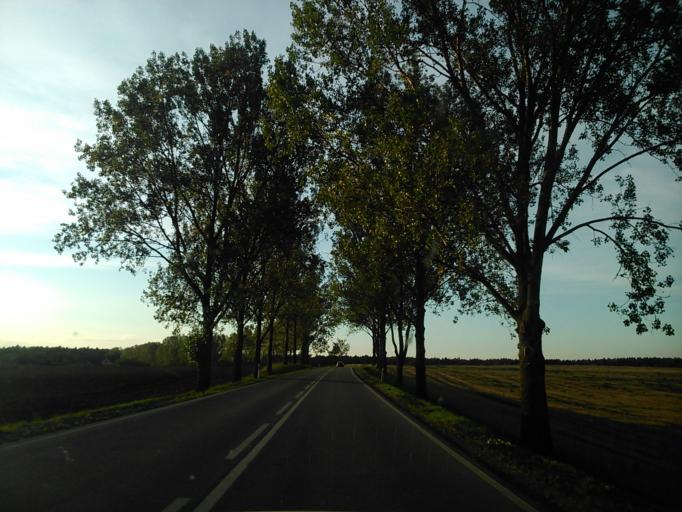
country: PL
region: Kujawsko-Pomorskie
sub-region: Powiat wabrzeski
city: Debowa Laka
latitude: 53.2546
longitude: 19.0226
